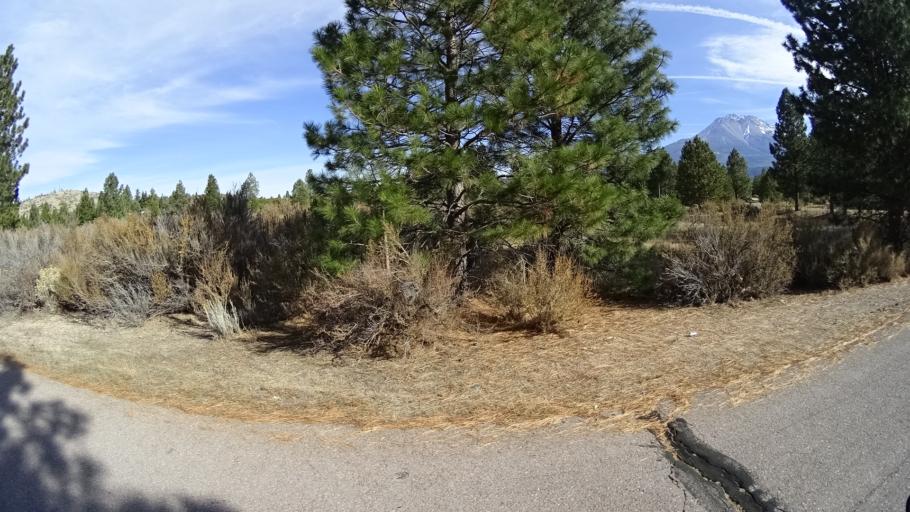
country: US
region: California
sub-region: Siskiyou County
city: Weed
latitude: 41.4226
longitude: -122.3985
